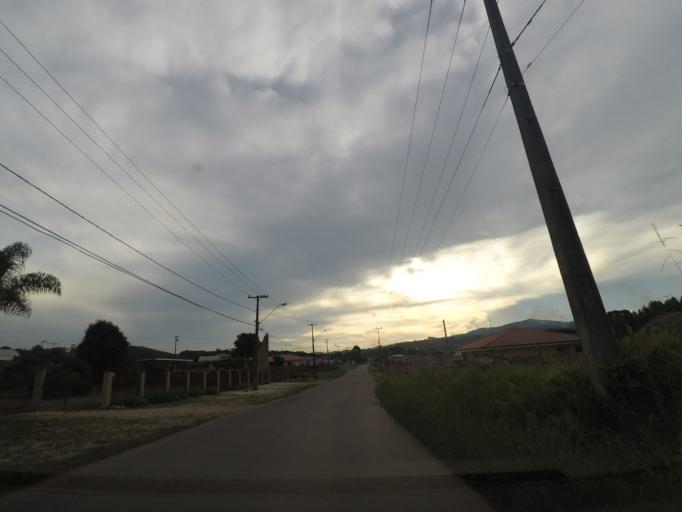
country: BR
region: Parana
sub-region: Colombo
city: Colombo
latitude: -25.2882
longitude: -49.1945
